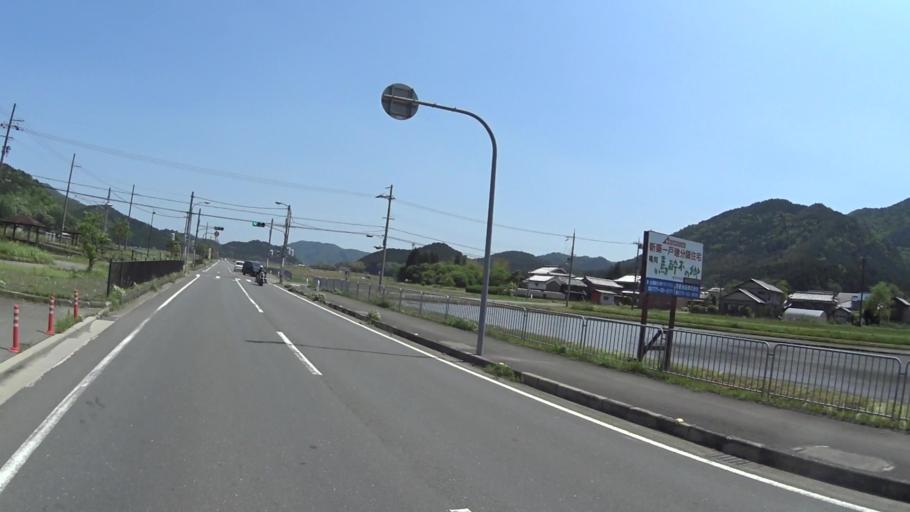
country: JP
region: Kyoto
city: Kameoka
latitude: 35.0523
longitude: 135.4723
